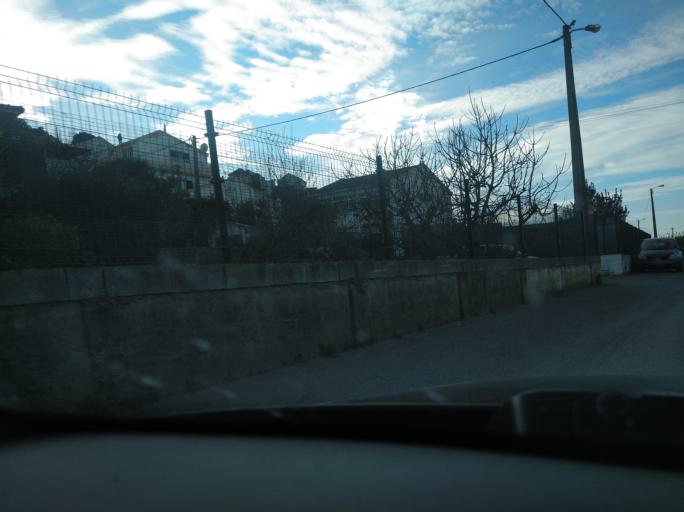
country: PT
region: Lisbon
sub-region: Loures
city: Unhos
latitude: 38.8357
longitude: -9.1245
